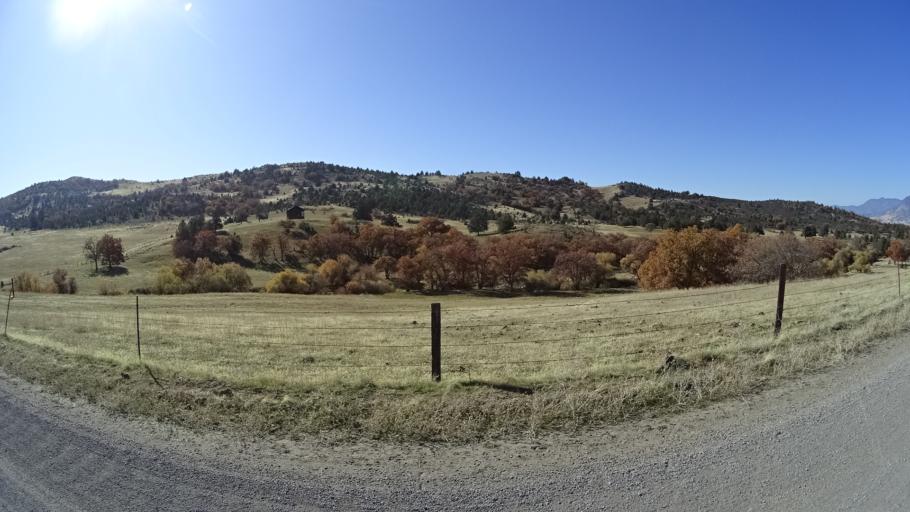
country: US
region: California
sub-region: Siskiyou County
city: Montague
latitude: 41.7965
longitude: -122.3657
